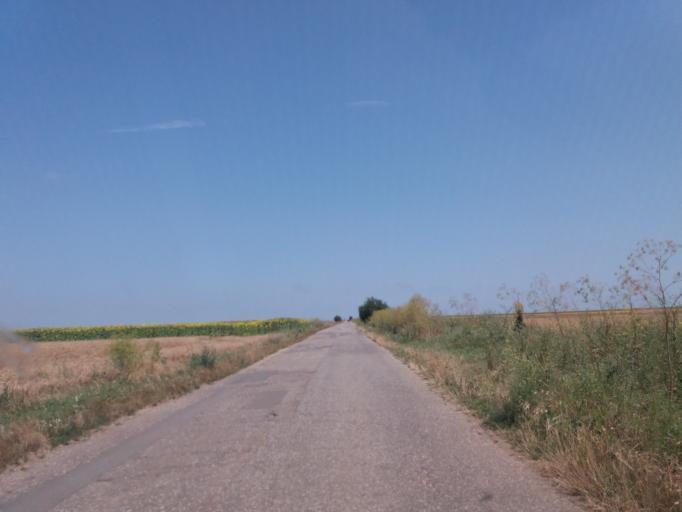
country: RO
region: Constanta
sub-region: Comuna Corbu
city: Corbu
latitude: 44.4240
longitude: 28.6686
